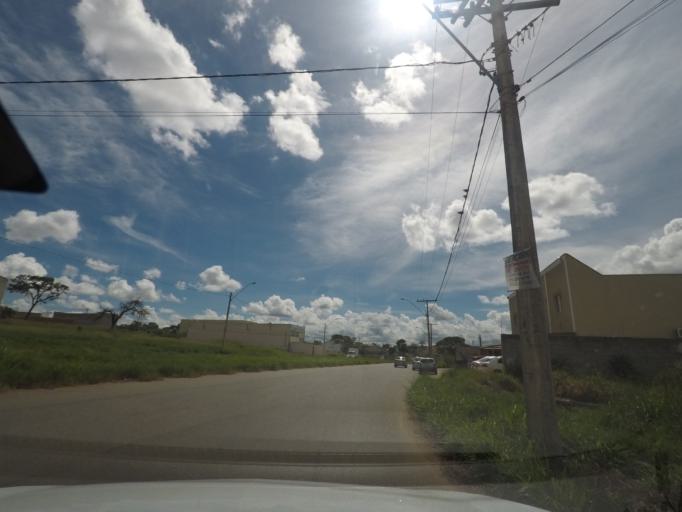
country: BR
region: Goias
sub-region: Goiania
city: Goiania
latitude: -16.7443
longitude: -49.3352
